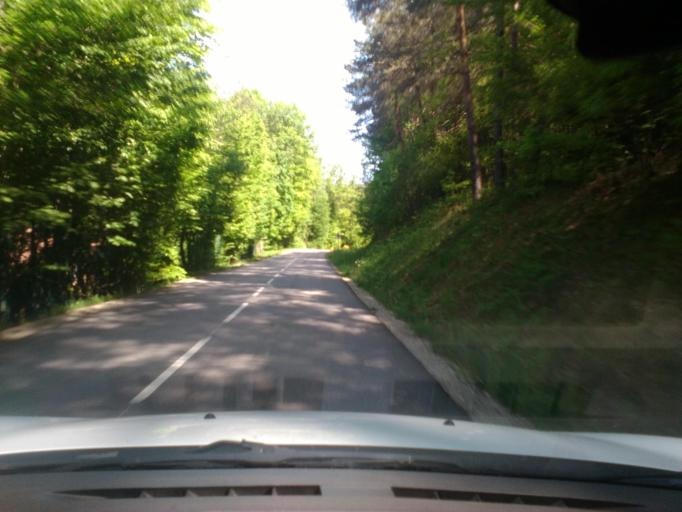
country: FR
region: Lorraine
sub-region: Departement des Vosges
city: Bruyeres
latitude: 48.2649
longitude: 6.7252
